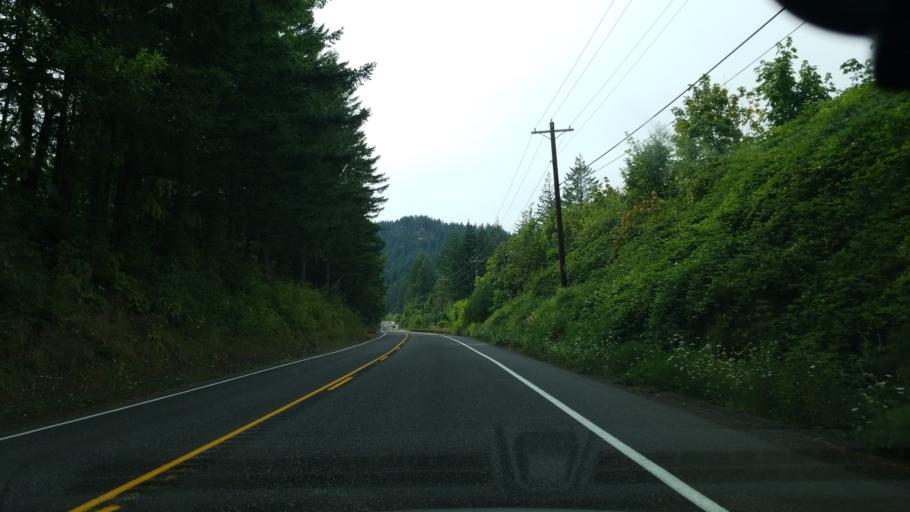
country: US
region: Washington
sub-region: Clark County
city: Washougal
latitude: 45.5885
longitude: -122.1700
